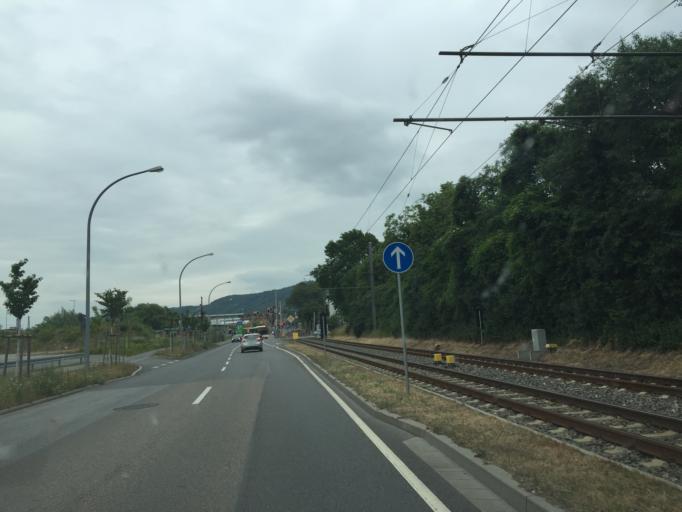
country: DE
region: Baden-Wuerttemberg
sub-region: Karlsruhe Region
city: Weinheim
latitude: 49.5450
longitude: 8.6629
